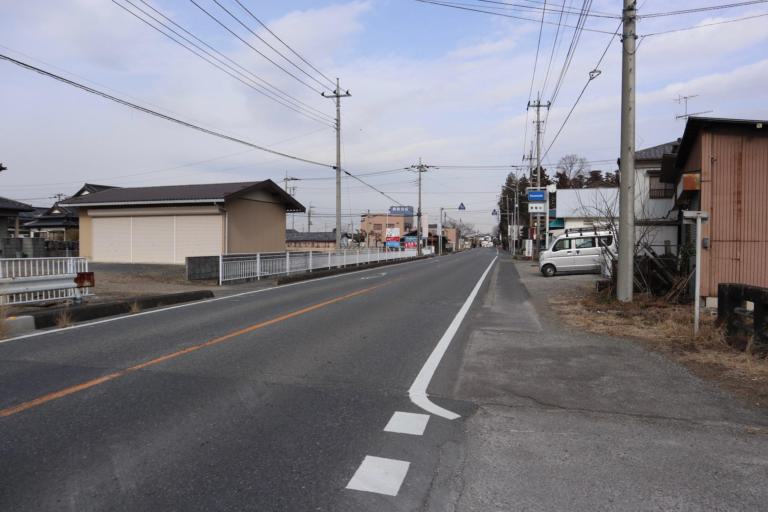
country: JP
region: Saitama
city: Gyoda
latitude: 36.1586
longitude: 139.4750
